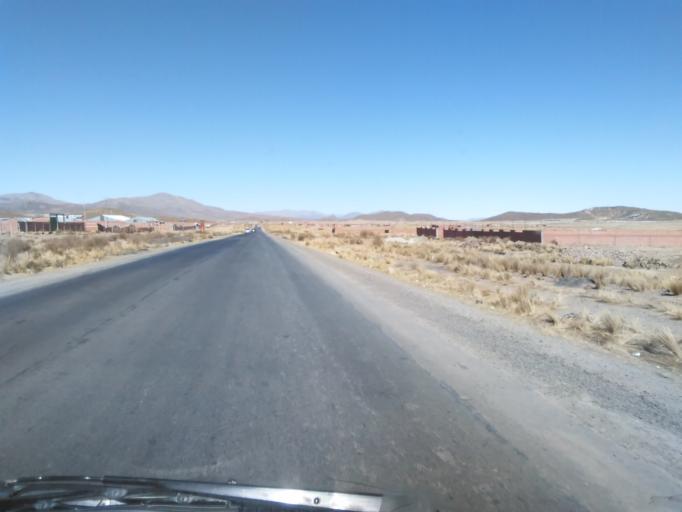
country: BO
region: Oruro
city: Oruro
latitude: -17.9977
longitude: -67.0445
